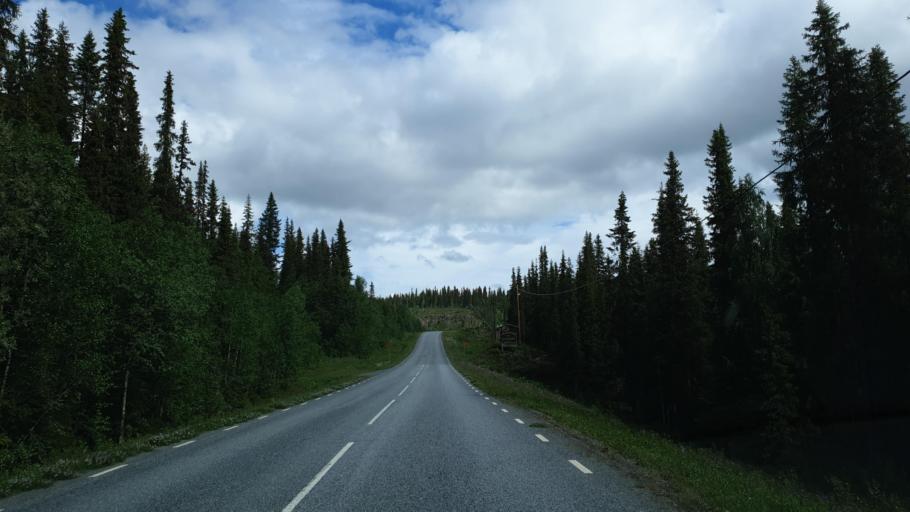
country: SE
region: Vaesterbotten
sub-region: Vilhelmina Kommun
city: Sjoberg
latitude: 65.2304
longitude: 15.9752
